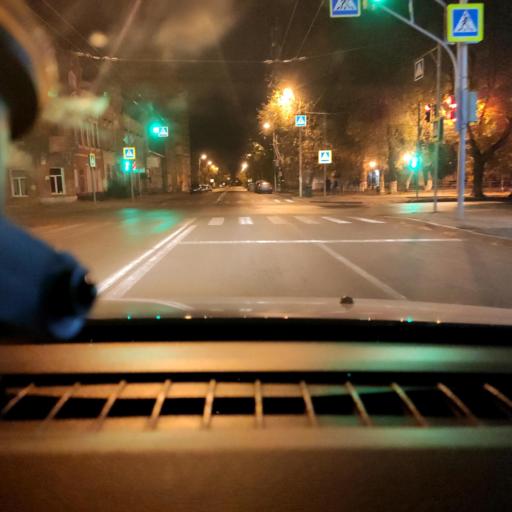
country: RU
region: Samara
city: Samara
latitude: 53.1849
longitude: 50.1019
